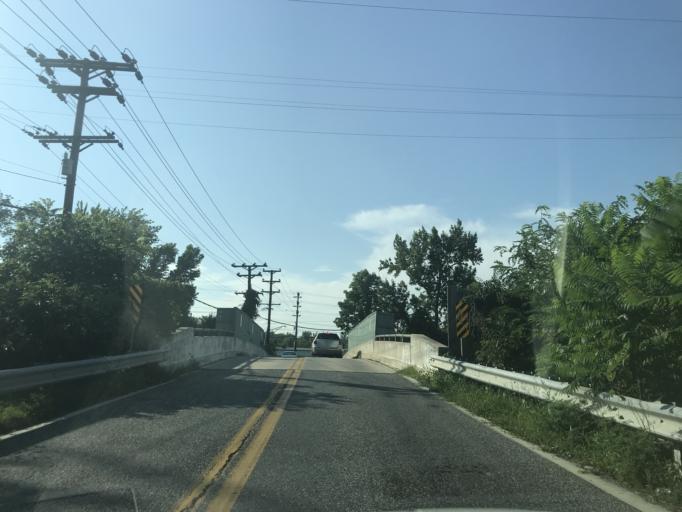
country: US
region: Maryland
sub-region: Harford County
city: Aberdeen
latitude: 39.5237
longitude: -76.1377
